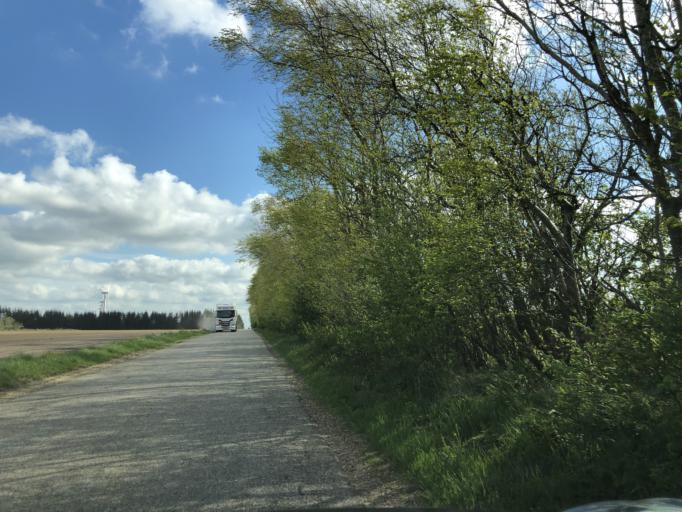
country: DK
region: Central Jutland
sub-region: Herning Kommune
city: Avlum
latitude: 56.2912
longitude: 8.6987
